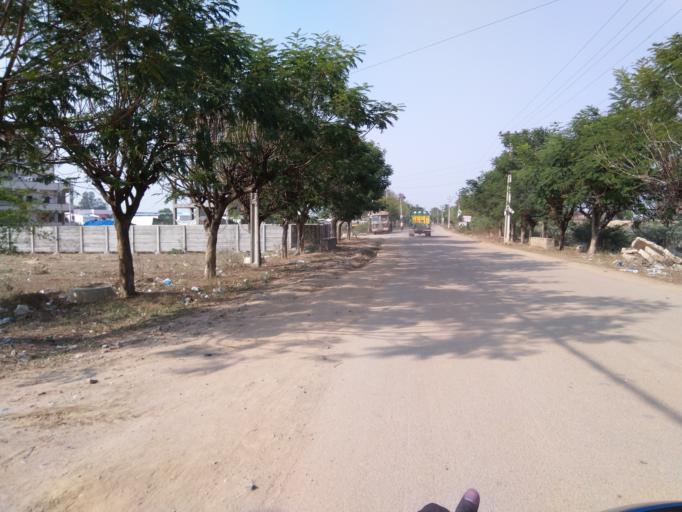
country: IN
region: Telangana
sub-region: Rangareddi
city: Quthbullapur
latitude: 17.5836
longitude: 78.4196
